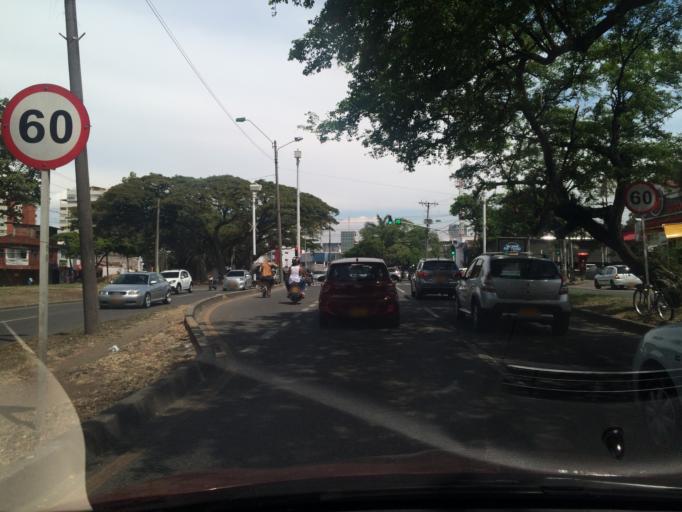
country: CO
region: Valle del Cauca
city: Cali
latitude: 3.4849
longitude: -76.5259
